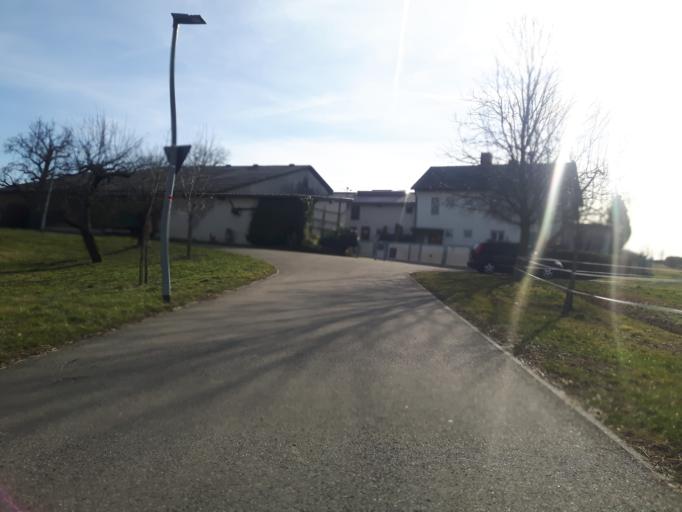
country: DE
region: Baden-Wuerttemberg
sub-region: Regierungsbezirk Stuttgart
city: Lehrensteinsfeld
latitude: 49.1354
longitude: 9.3626
